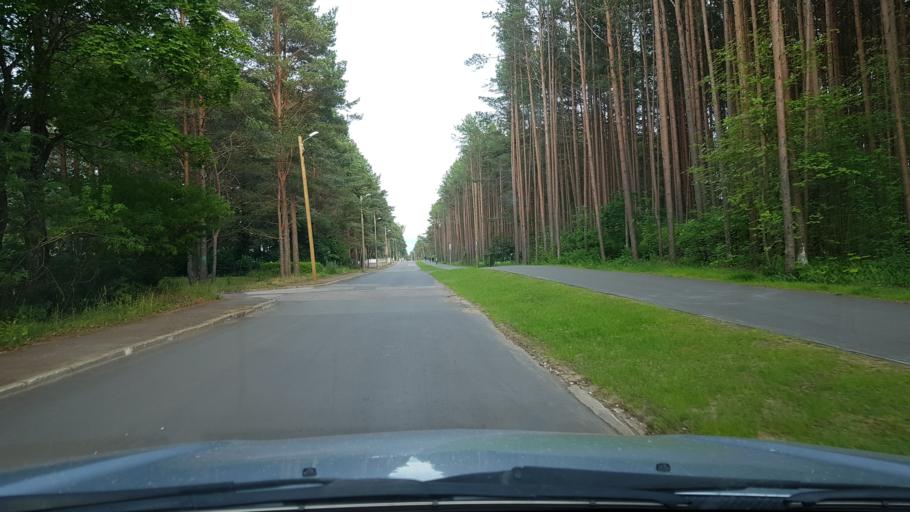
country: EE
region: Ida-Virumaa
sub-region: Narva-Joesuu linn
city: Narva-Joesuu
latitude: 59.4564
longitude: 28.0423
